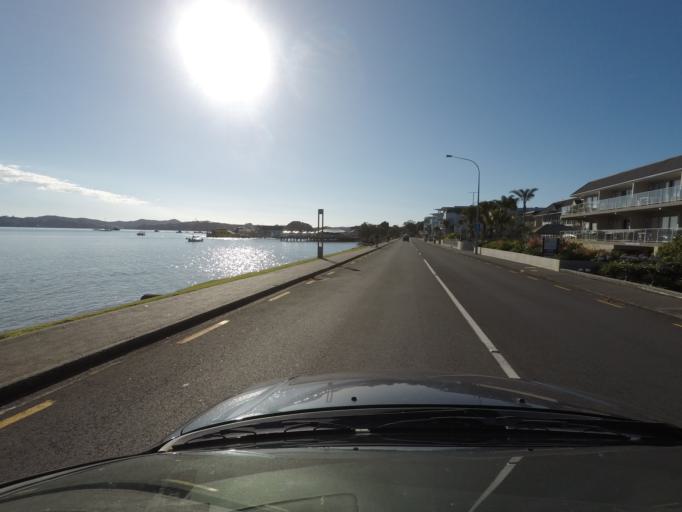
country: NZ
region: Northland
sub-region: Far North District
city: Paihia
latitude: -35.2800
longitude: 174.0901
